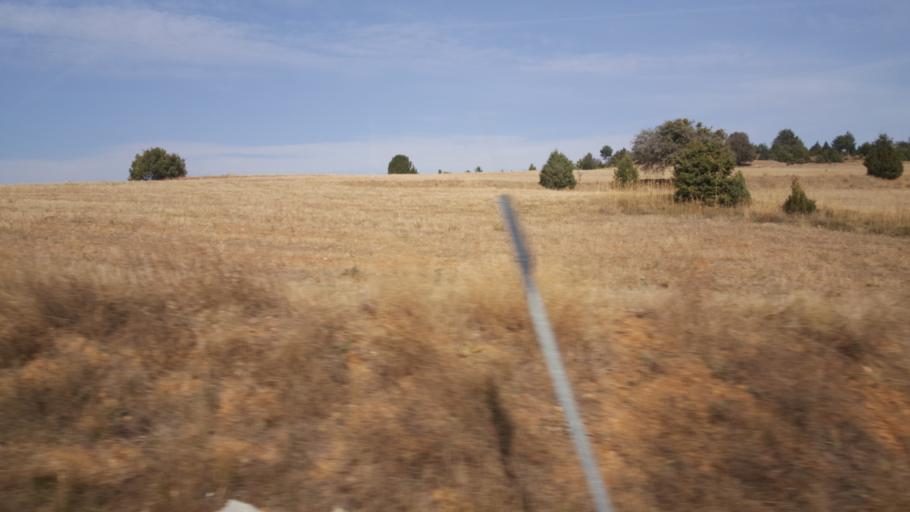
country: TR
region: Eskisehir
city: Mihaliccik
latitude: 39.9628
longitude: 31.3888
